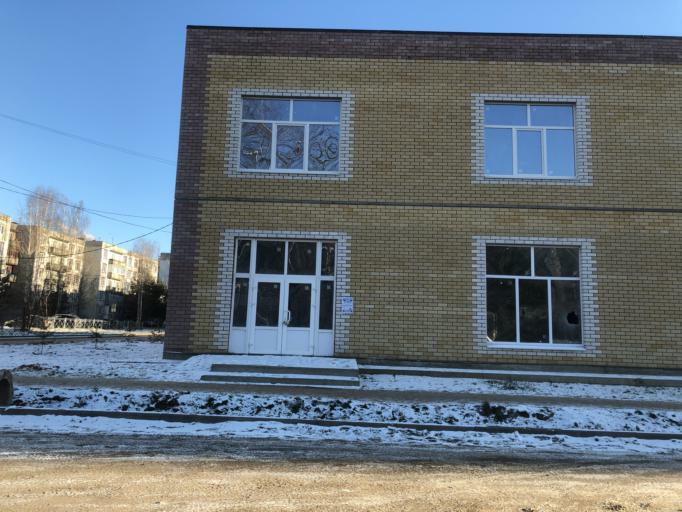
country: RU
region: Tverskaya
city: Rzhev
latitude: 56.2589
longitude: 34.3503
